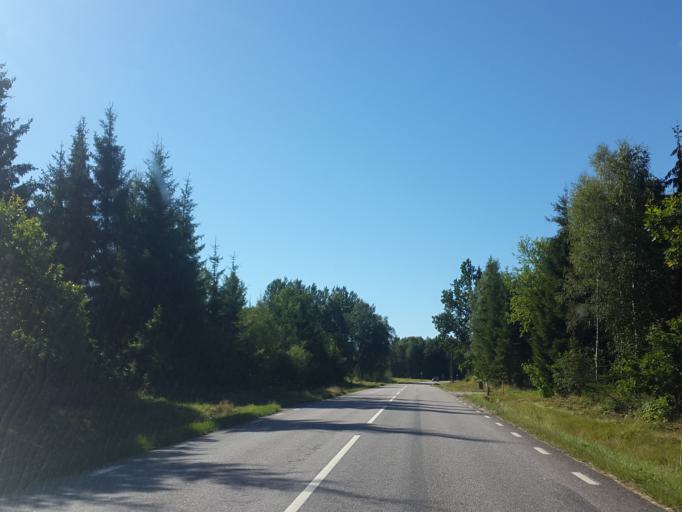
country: SE
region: Vaestra Goetaland
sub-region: Herrljunga Kommun
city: Herrljunga
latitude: 58.0638
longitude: 13.0434
